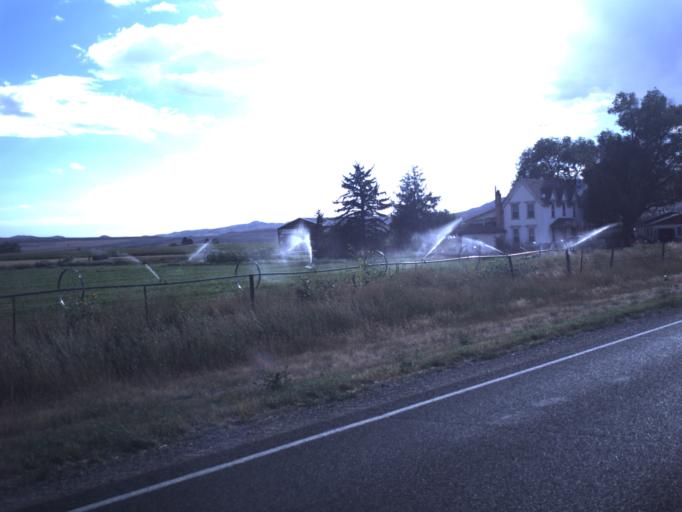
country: US
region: Utah
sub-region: Cache County
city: Lewiston
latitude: 41.9755
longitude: -111.9076
